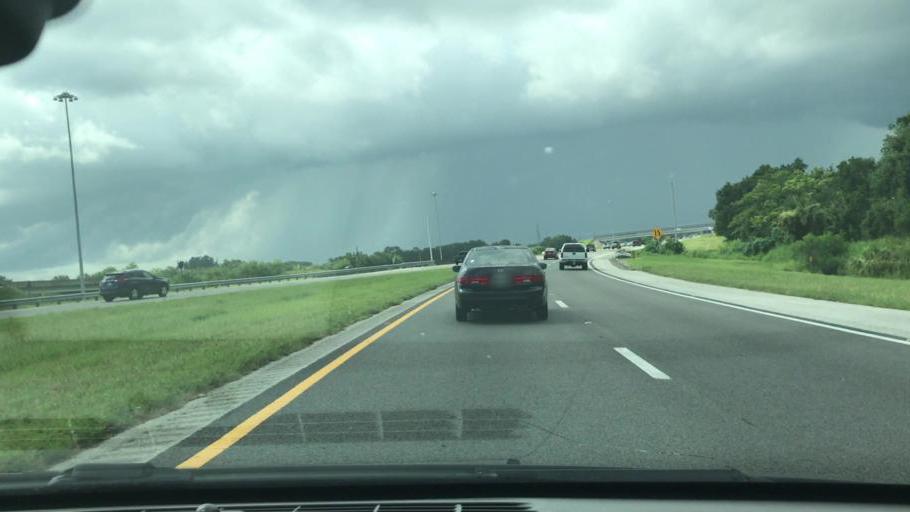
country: US
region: Florida
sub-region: Manatee County
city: Ellenton
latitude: 27.5813
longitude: -82.5152
